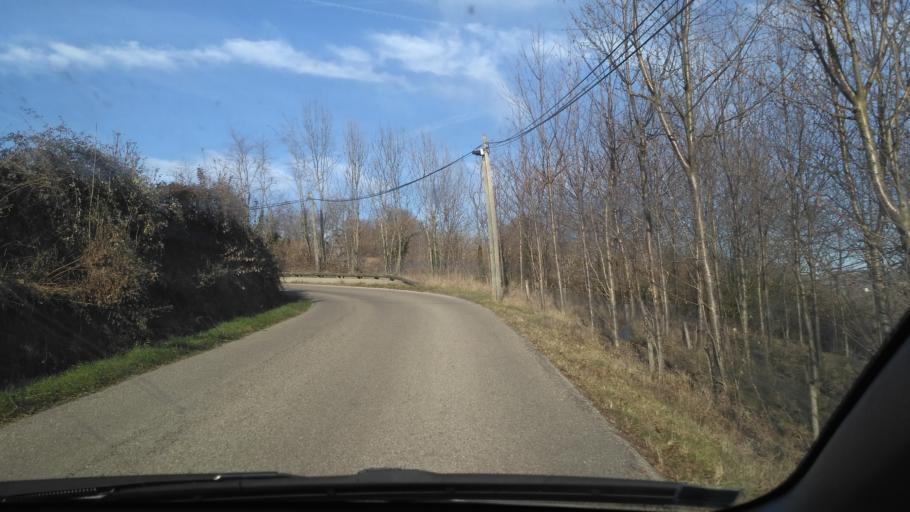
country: FR
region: Rhone-Alpes
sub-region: Departement de l'Isere
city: Saint-Antoine-l'Abbaye
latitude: 45.1784
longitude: 5.2119
